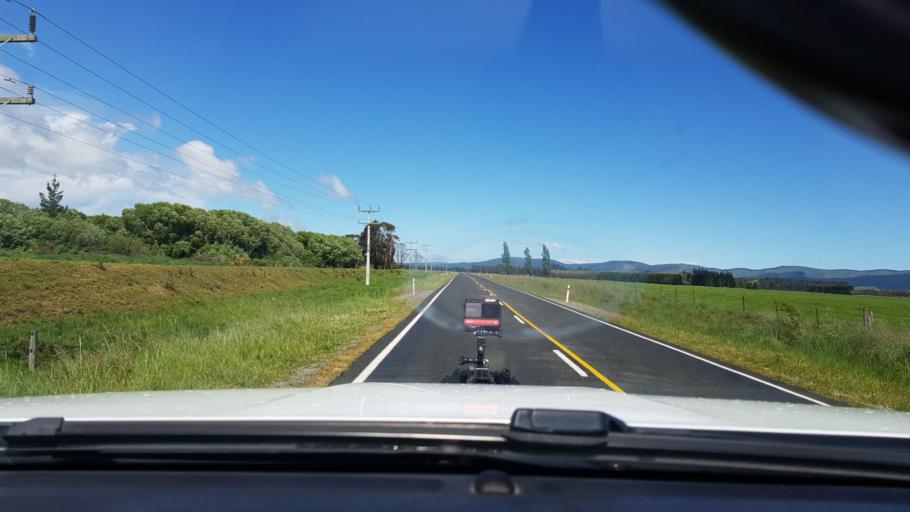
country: NZ
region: Southland
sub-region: Southland District
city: Winton
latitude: -45.8457
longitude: 168.3648
